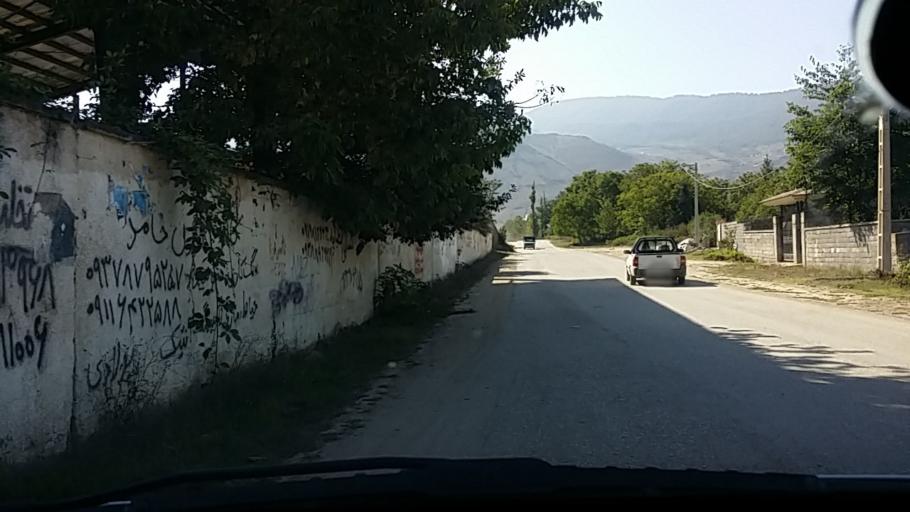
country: IR
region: Mazandaran
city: `Abbasabad
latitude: 36.5002
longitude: 51.1635
